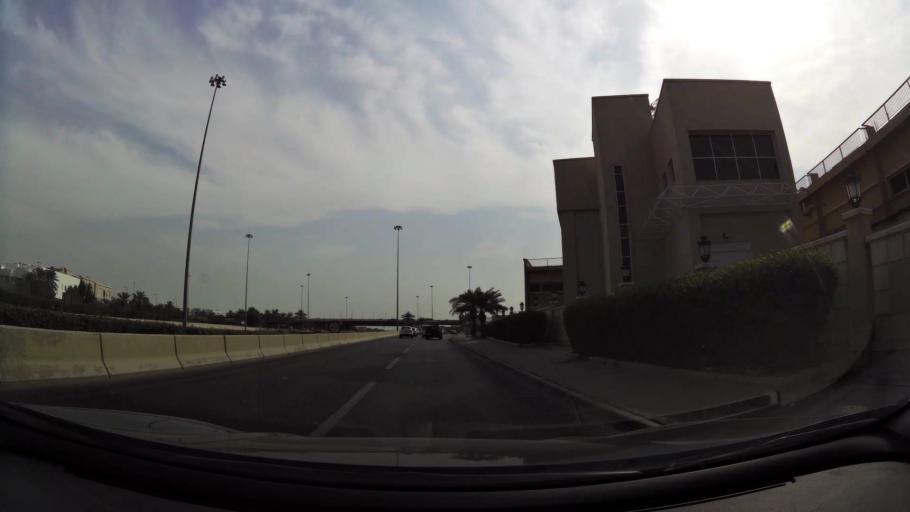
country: KW
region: Al Asimah
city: Ash Shamiyah
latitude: 29.3207
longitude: 47.9738
